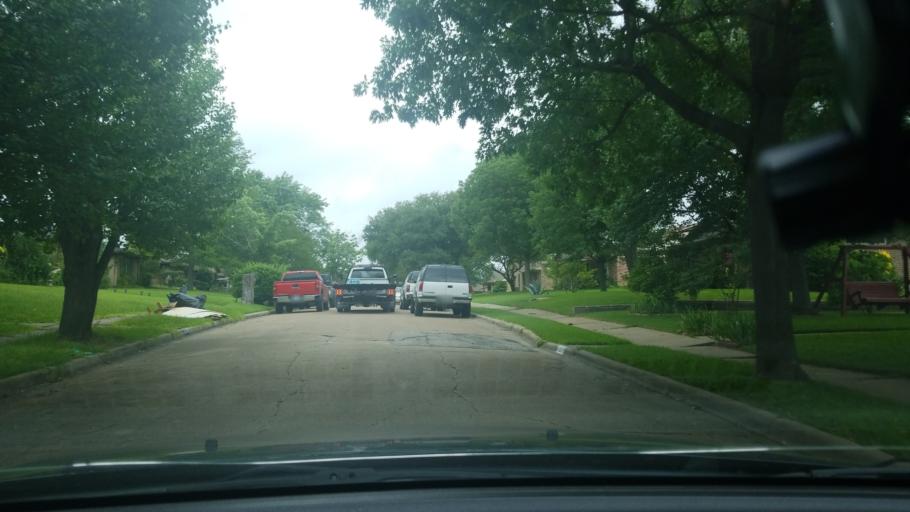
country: US
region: Texas
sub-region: Dallas County
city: Mesquite
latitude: 32.7805
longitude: -96.6326
